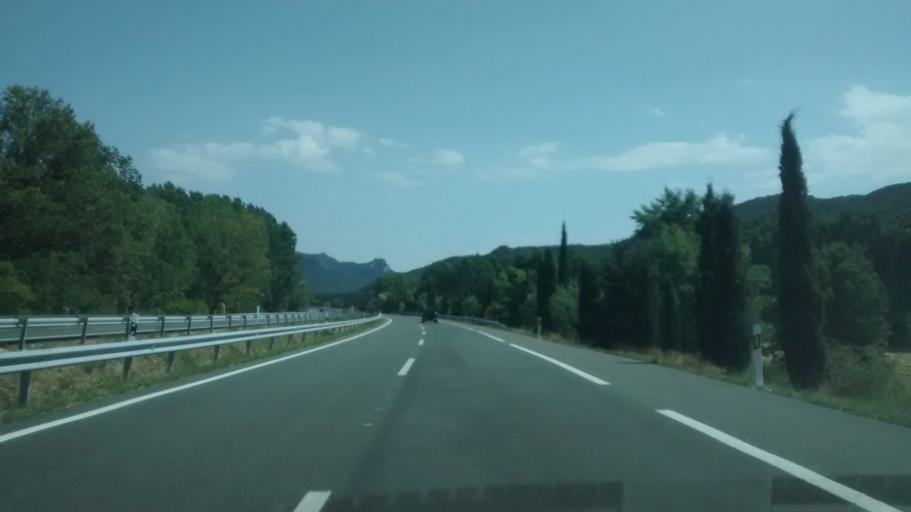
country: ES
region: Basque Country
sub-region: Provincia de Alava
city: Zambrana
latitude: 42.6457
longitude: -2.8772
